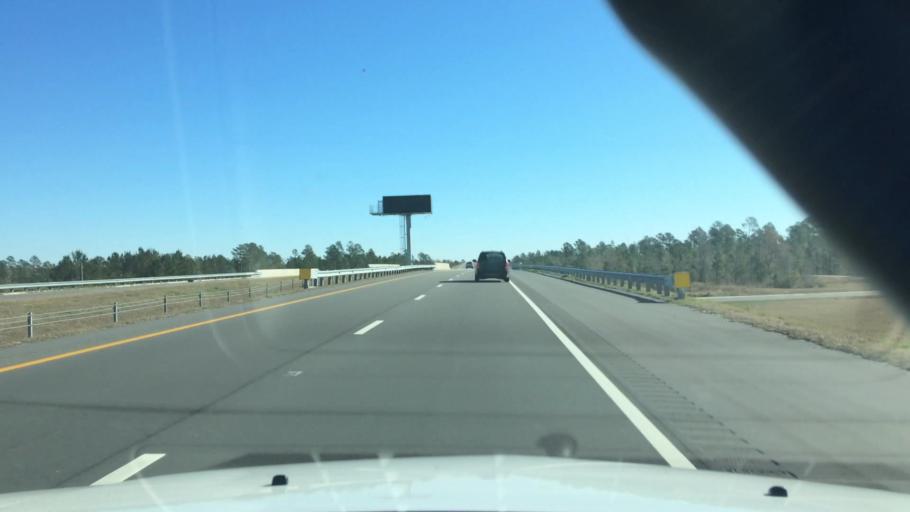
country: US
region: North Carolina
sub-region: Brunswick County
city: Navassa
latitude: 34.2729
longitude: -78.0189
